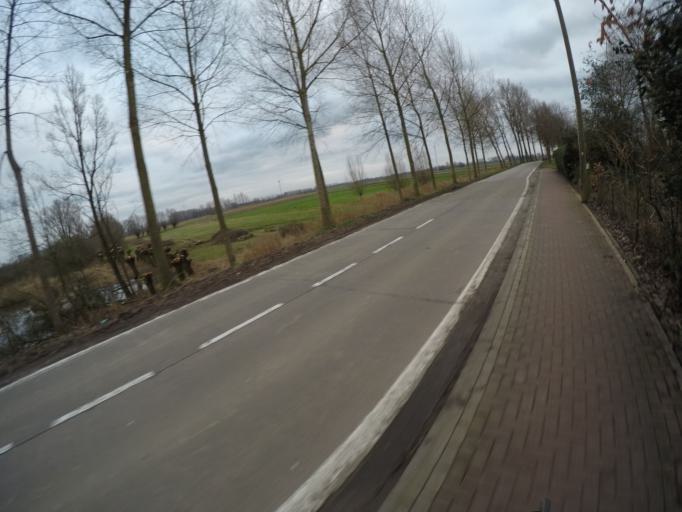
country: BE
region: Flanders
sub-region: Provincie Oost-Vlaanderen
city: Sint-Gillis-Waas
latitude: 51.2424
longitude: 4.1468
